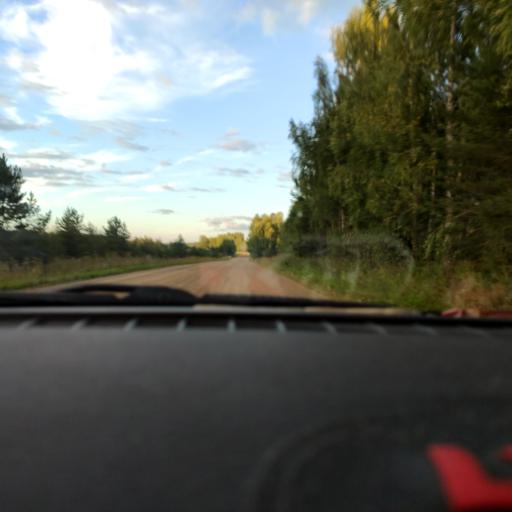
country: RU
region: Perm
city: Pavlovskiy
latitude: 57.9938
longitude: 54.8871
